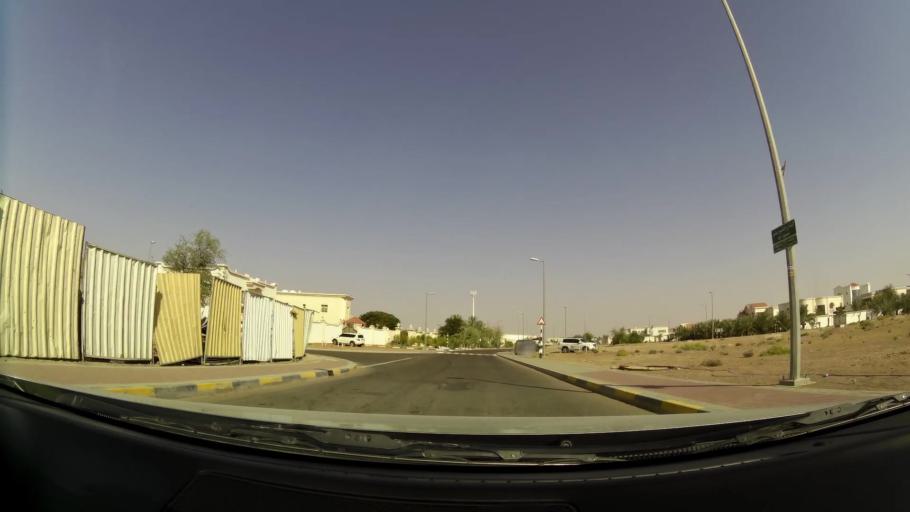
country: OM
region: Al Buraimi
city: Al Buraymi
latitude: 24.3446
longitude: 55.7964
